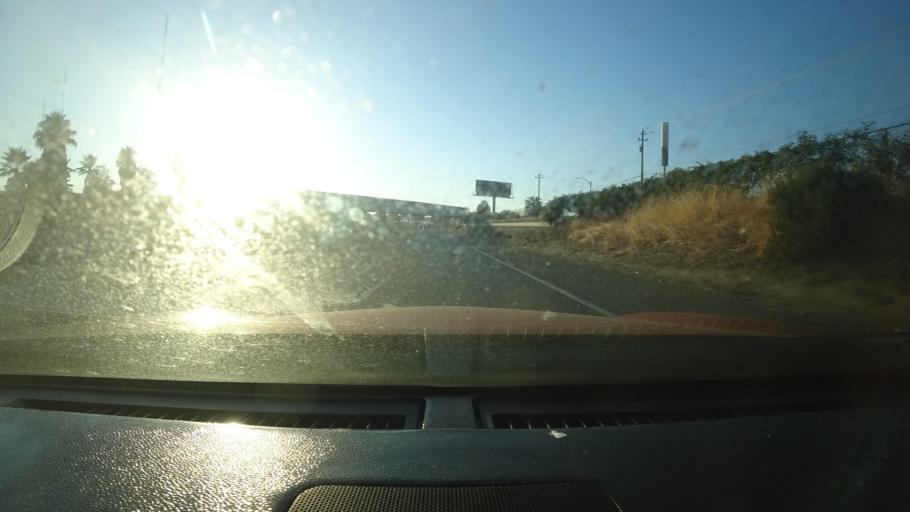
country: US
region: California
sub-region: Santa Clara County
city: San Jose
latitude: 37.3579
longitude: -121.8701
